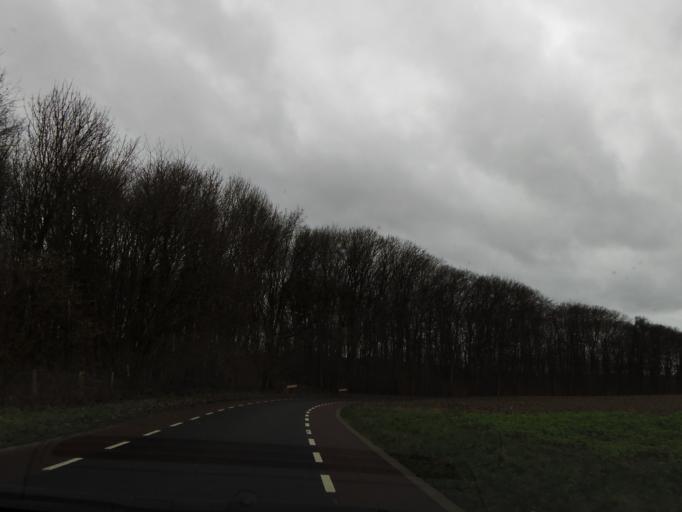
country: NL
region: Limburg
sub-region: Eijsden-Margraten
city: Margraten
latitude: 50.8102
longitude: 5.8089
